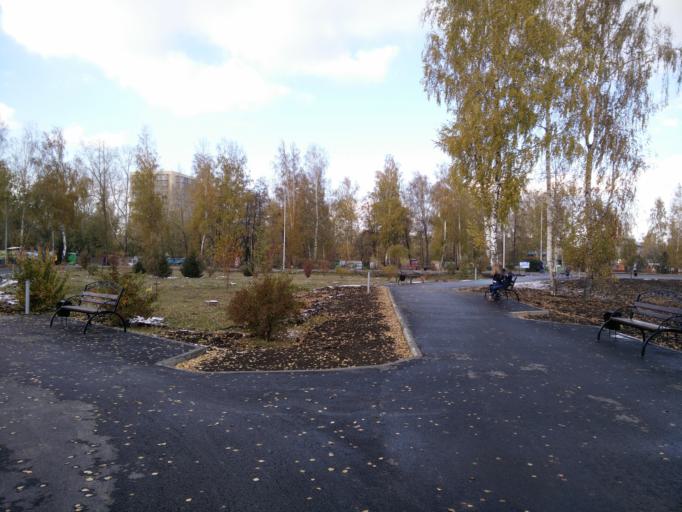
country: RU
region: Novosibirsk
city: Berdsk
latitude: 54.7568
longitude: 83.1027
